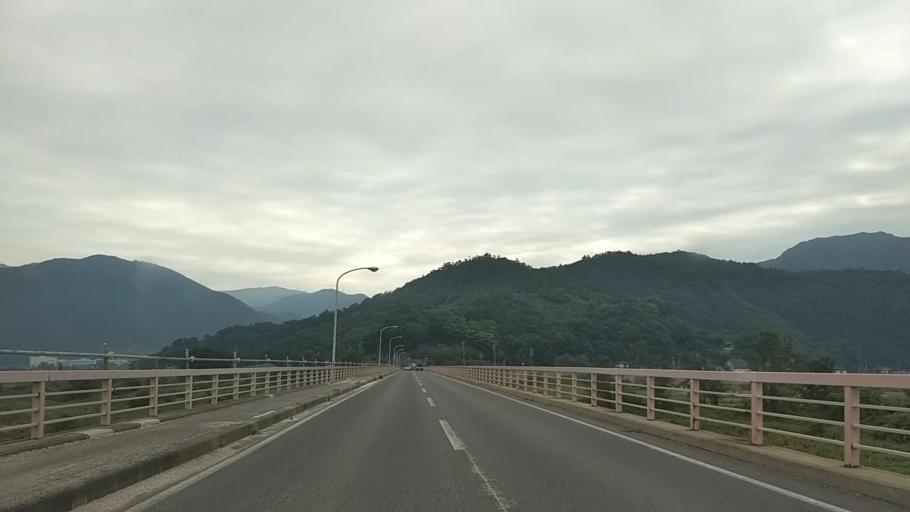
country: JP
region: Nagano
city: Nagano-shi
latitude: 36.6066
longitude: 138.2223
